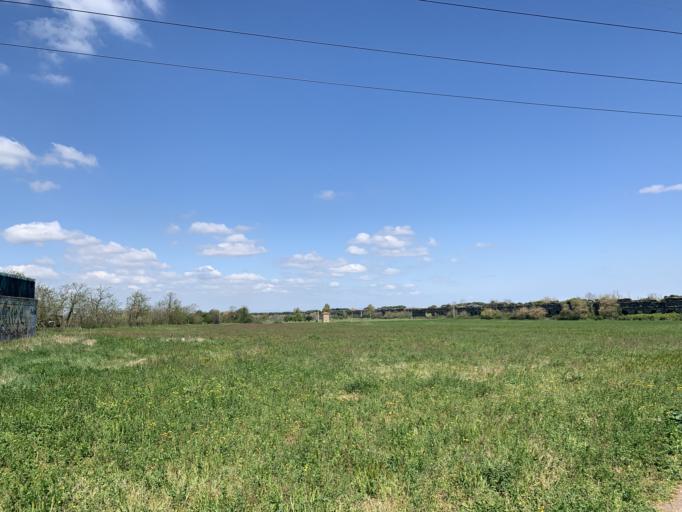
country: IT
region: Latium
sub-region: Citta metropolitana di Roma Capitale
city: Ciampino
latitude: 41.8357
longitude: 12.5693
